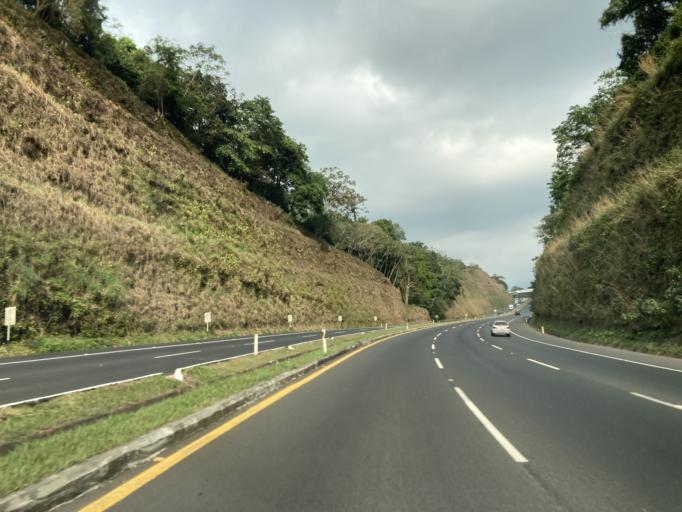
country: GT
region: Escuintla
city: Palin
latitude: 14.3892
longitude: -90.7649
